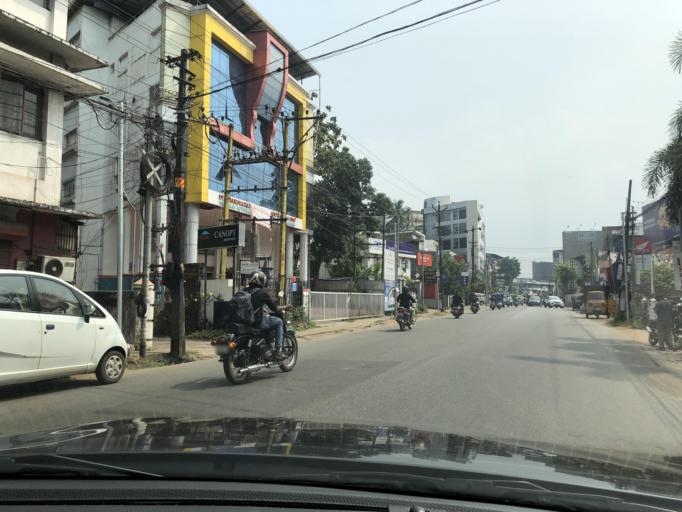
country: IN
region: Kerala
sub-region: Kozhikode
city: Kozhikode
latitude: 11.2749
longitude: 75.7732
